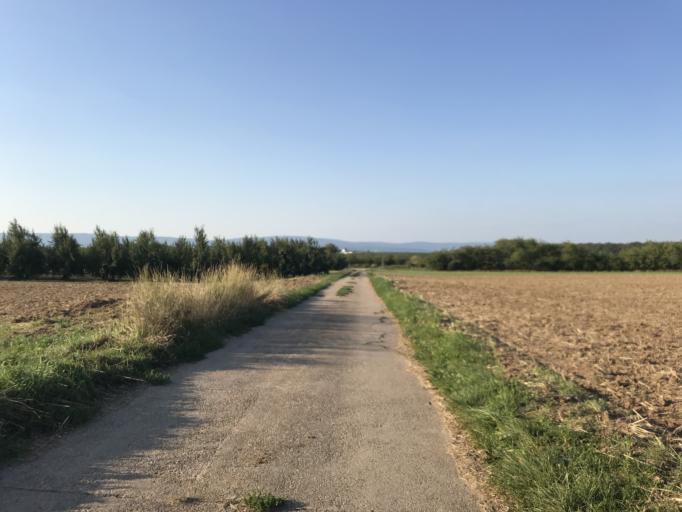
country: DE
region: Rheinland-Pfalz
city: Essenheim
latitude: 49.9551
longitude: 8.1511
